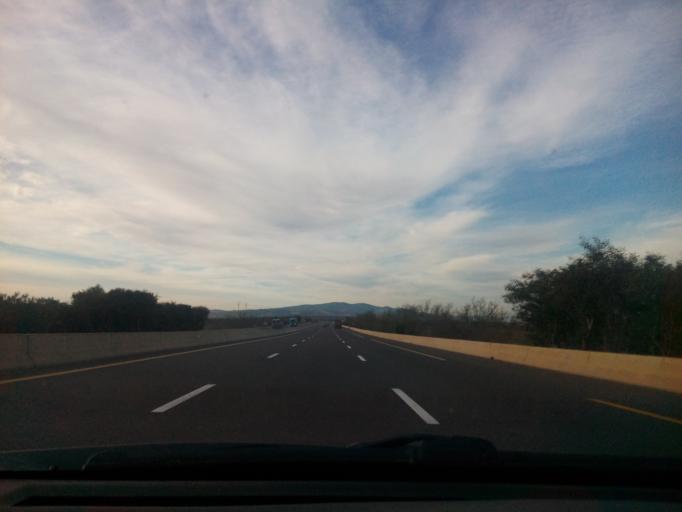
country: DZ
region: Mascara
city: Mascara
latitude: 35.6392
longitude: 0.0921
